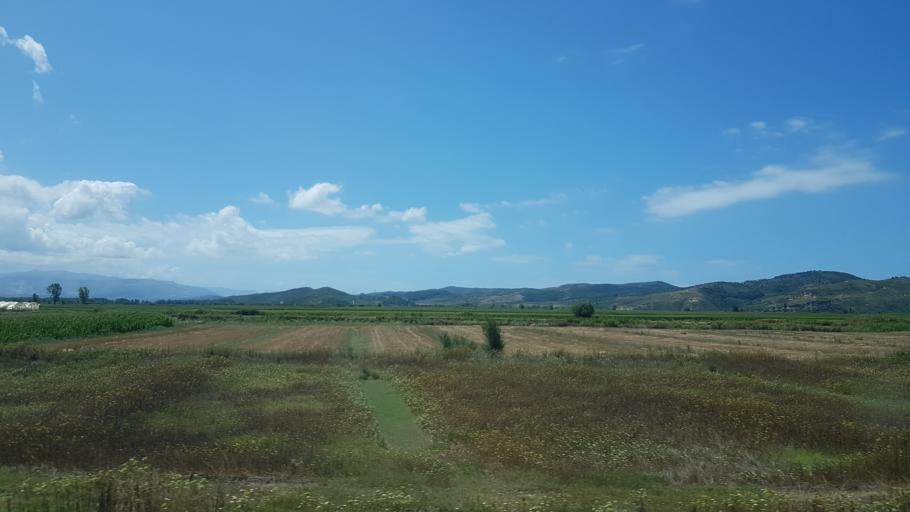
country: AL
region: Fier
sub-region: Rrethi i Fierit
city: Cakran
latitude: 40.6006
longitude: 19.5614
